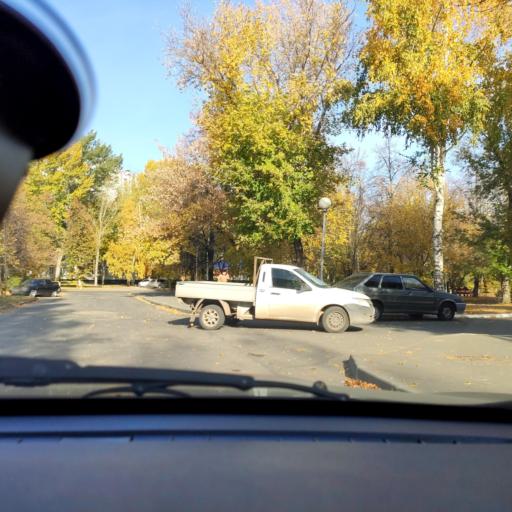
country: RU
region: Samara
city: Tol'yatti
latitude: 53.5125
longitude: 49.2657
